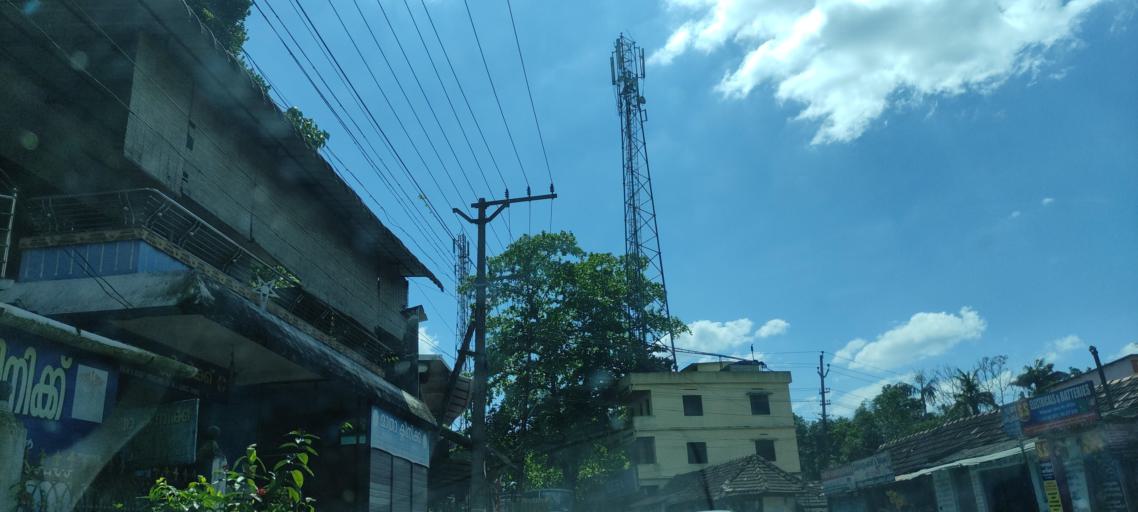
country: IN
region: Kerala
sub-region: Pattanamtitta
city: Adur
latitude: 9.1222
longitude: 76.7001
